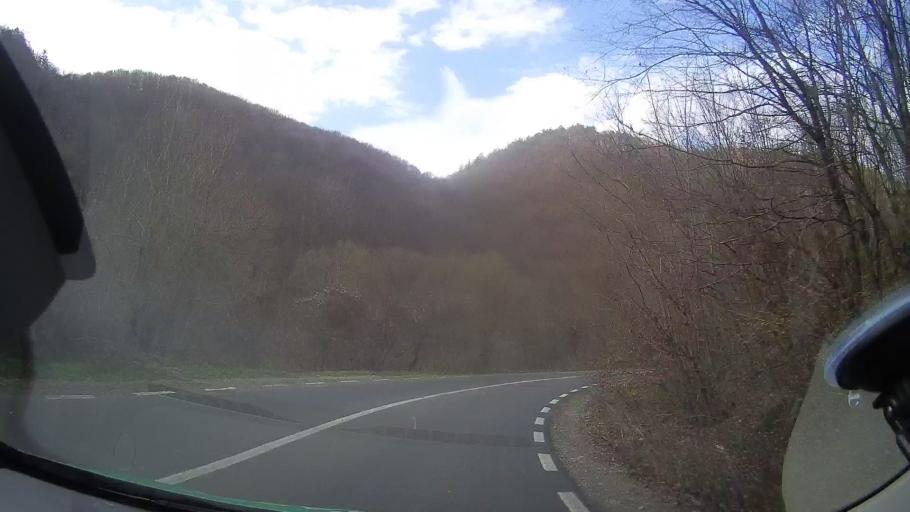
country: RO
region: Cluj
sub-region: Comuna Baisoara
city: Baisoara
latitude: 46.5857
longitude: 23.4434
